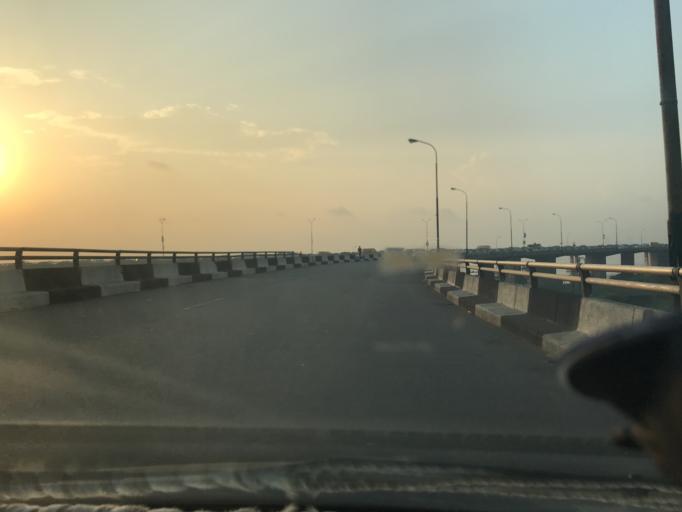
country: NG
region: Lagos
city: Ebute Metta
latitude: 6.4870
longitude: 3.3936
